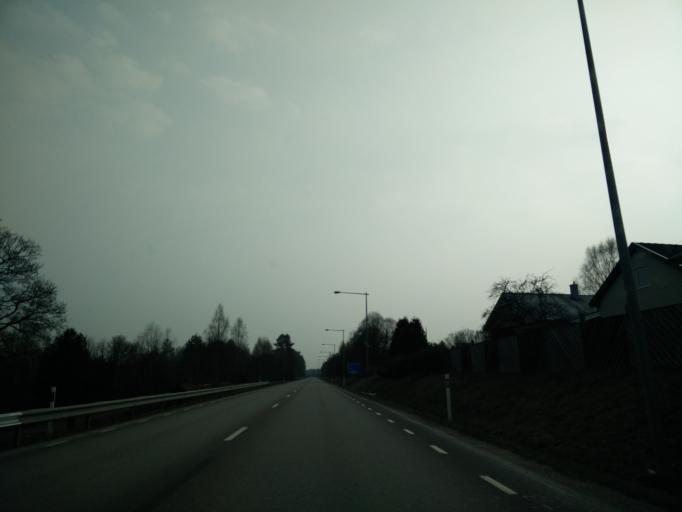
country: SE
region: Vaermland
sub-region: Forshaga Kommun
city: Forshaga
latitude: 59.5156
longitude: 13.4428
